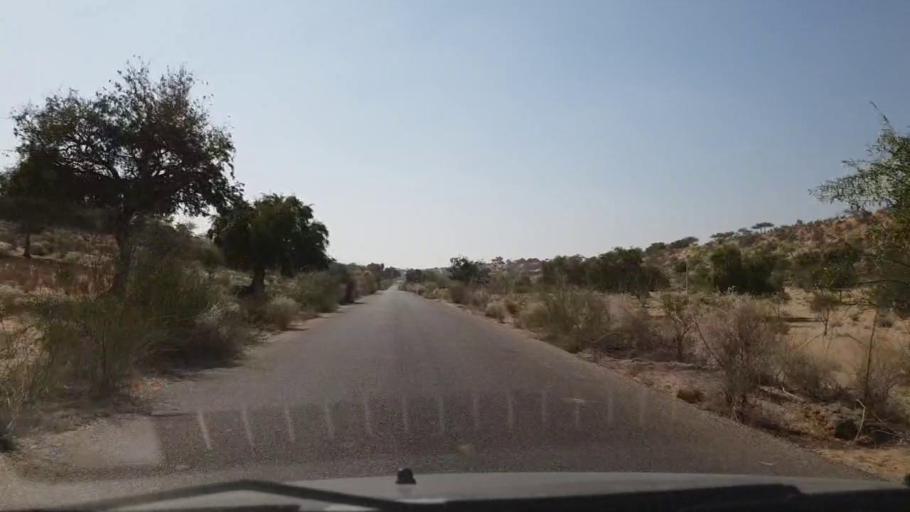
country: PK
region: Sindh
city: Diplo
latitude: 24.5504
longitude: 69.6559
